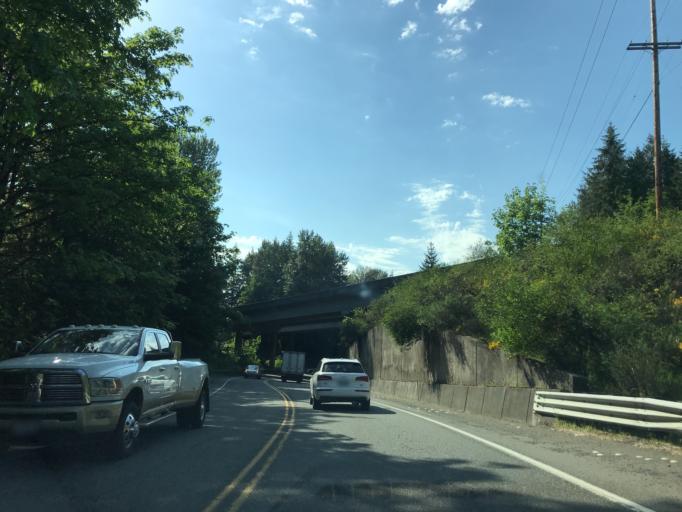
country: US
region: Washington
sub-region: King County
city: Hobart
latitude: 47.4352
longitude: -121.9739
